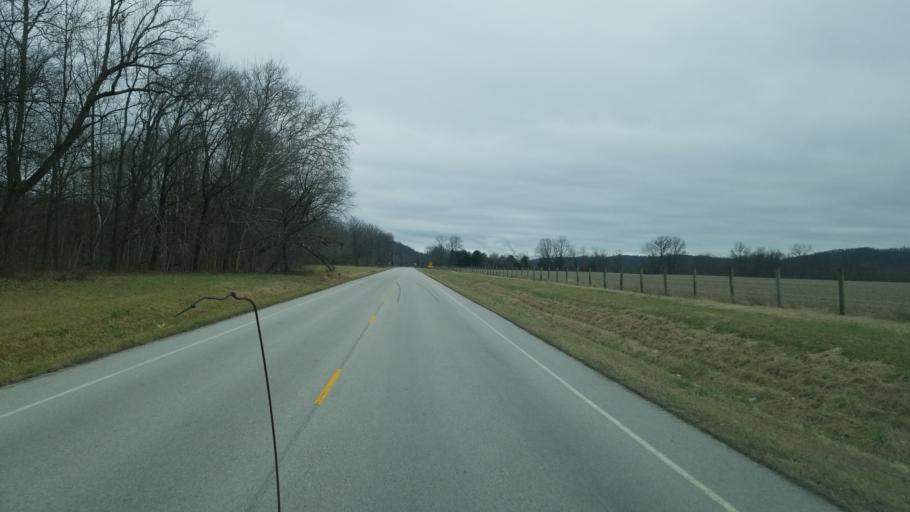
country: US
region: Kentucky
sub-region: Bracken County
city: Augusta
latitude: 38.7850
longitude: -83.9330
